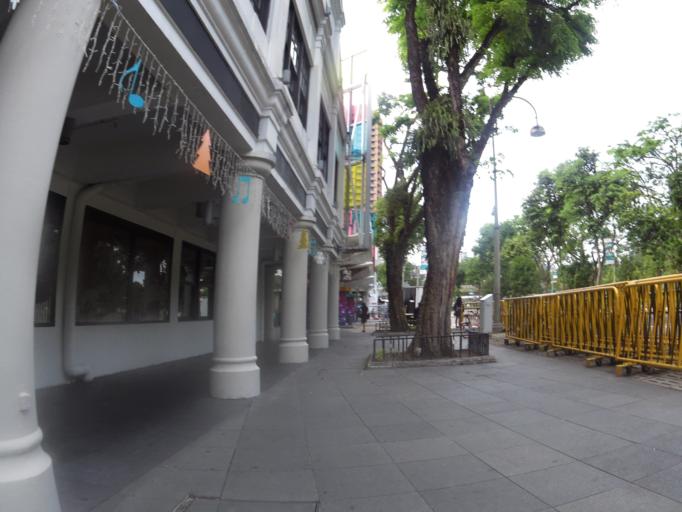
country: SG
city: Singapore
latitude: 1.2910
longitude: 103.8462
